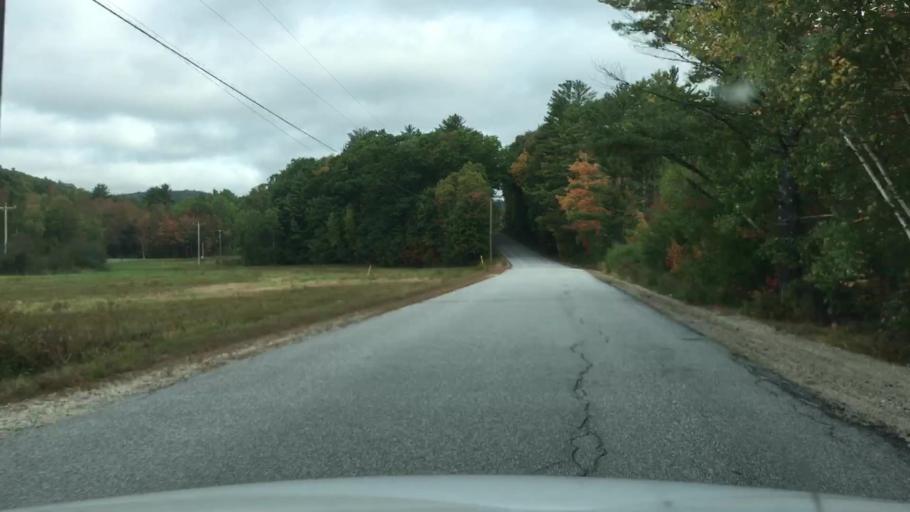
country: US
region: Maine
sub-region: Cumberland County
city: Harrison
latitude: 44.2519
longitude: -70.7226
